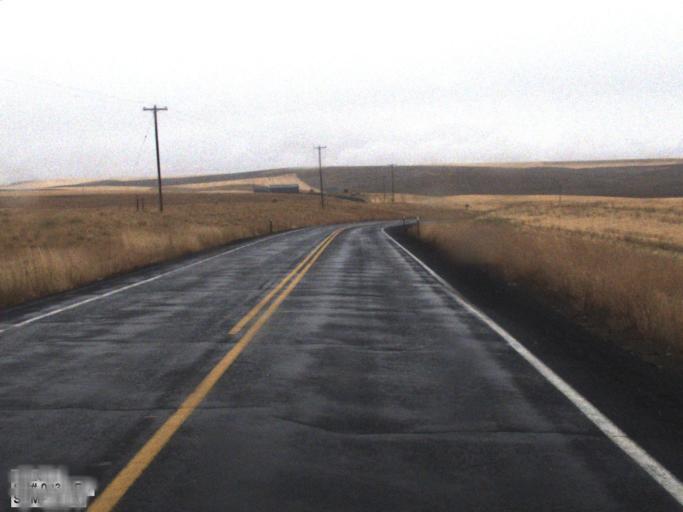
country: US
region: Washington
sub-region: Lincoln County
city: Davenport
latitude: 47.4785
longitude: -118.1964
